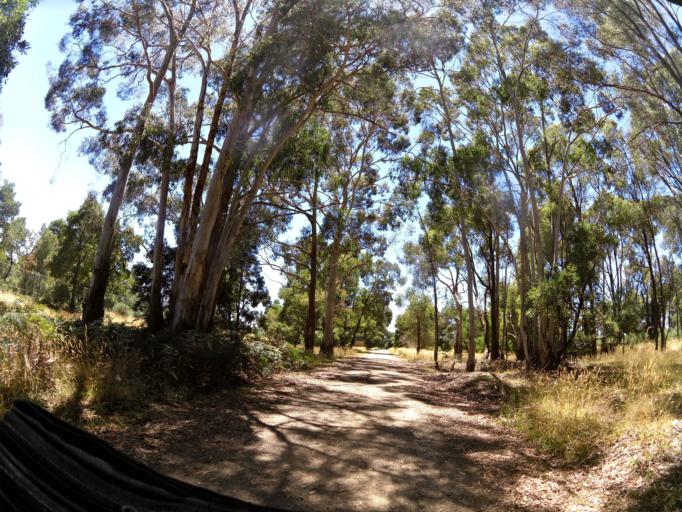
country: AU
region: Victoria
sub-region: Ballarat North
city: Delacombe
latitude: -37.6222
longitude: 143.7047
